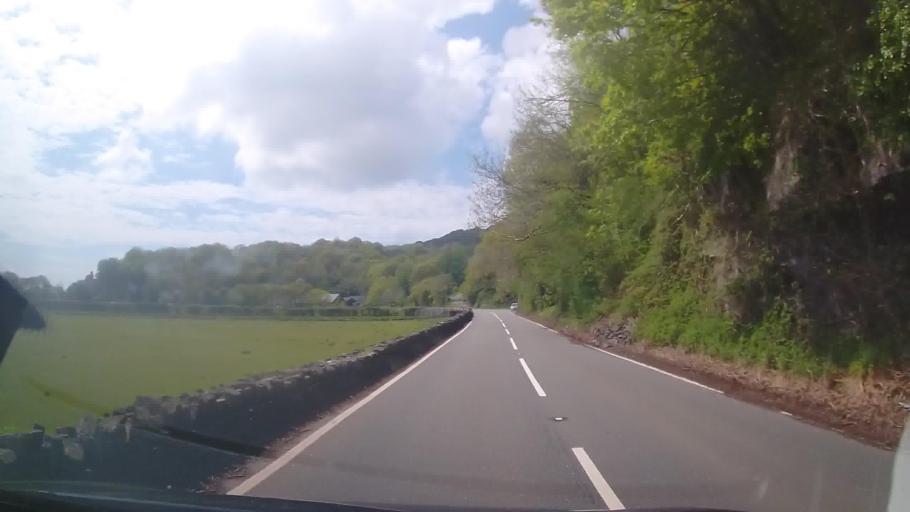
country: GB
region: Wales
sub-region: Gwynedd
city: Porthmadog
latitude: 52.9483
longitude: -4.1107
